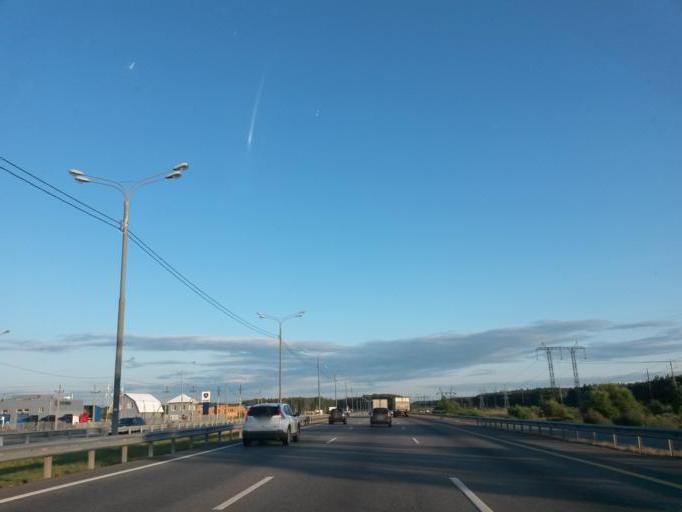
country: RU
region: Moskovskaya
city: Vostryakovo
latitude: 55.3742
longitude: 37.7802
